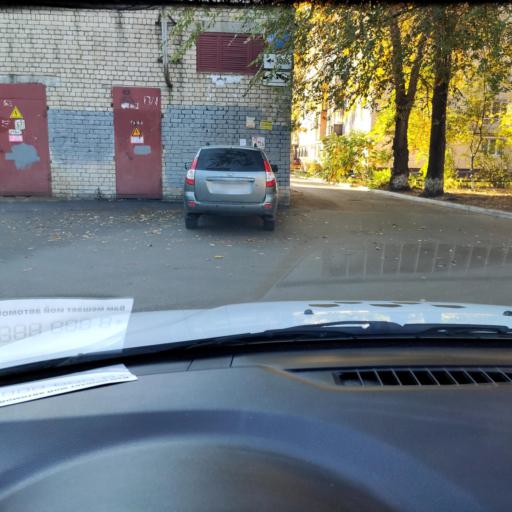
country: RU
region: Samara
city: Tol'yatti
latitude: 53.5105
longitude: 49.4253
